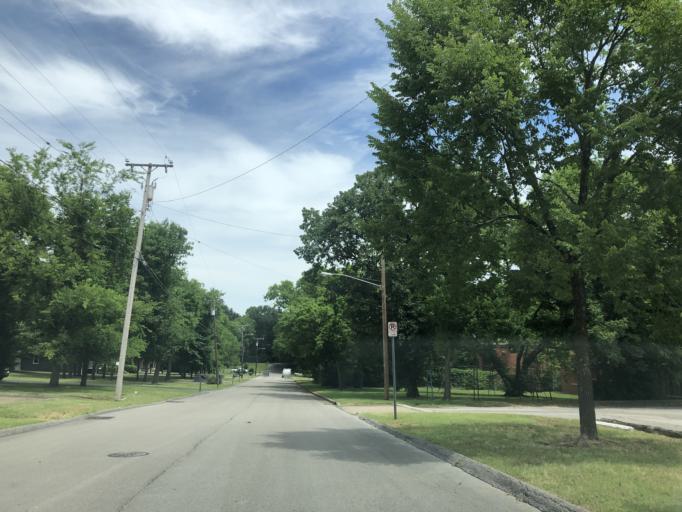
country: US
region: Tennessee
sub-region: Davidson County
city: Oak Hill
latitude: 36.1136
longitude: -86.8016
